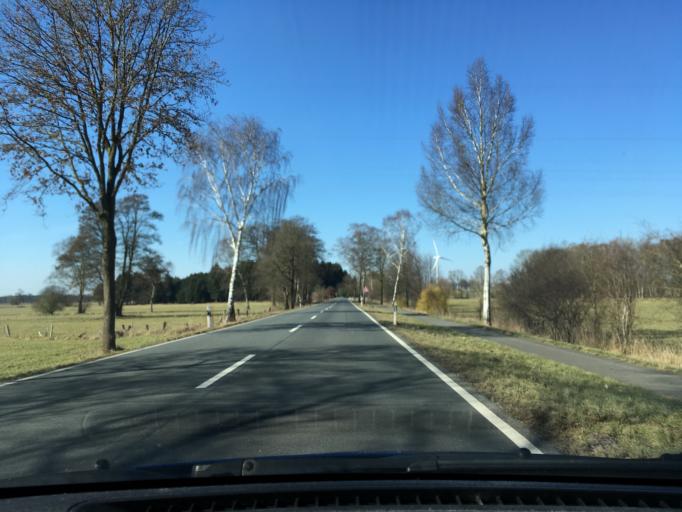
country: DE
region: Lower Saxony
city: Hemslingen
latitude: 53.0708
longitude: 9.6422
